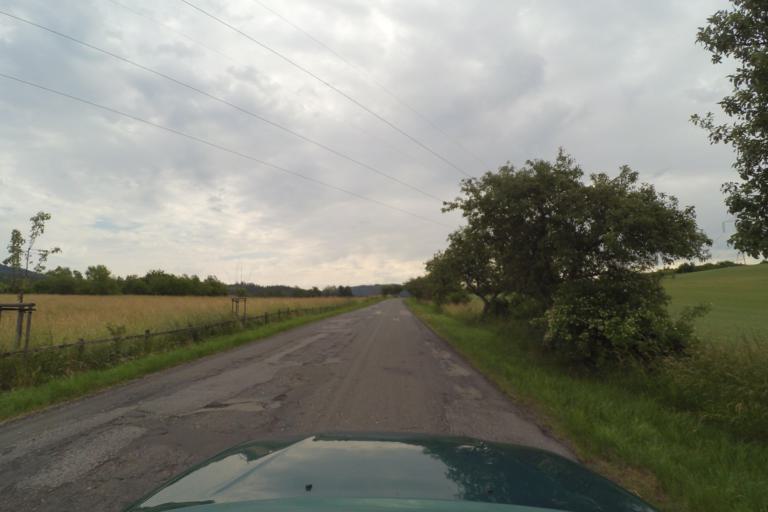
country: CZ
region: Liberecky
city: Hodkovice nad Mohelkou
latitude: 50.6698
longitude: 15.0736
